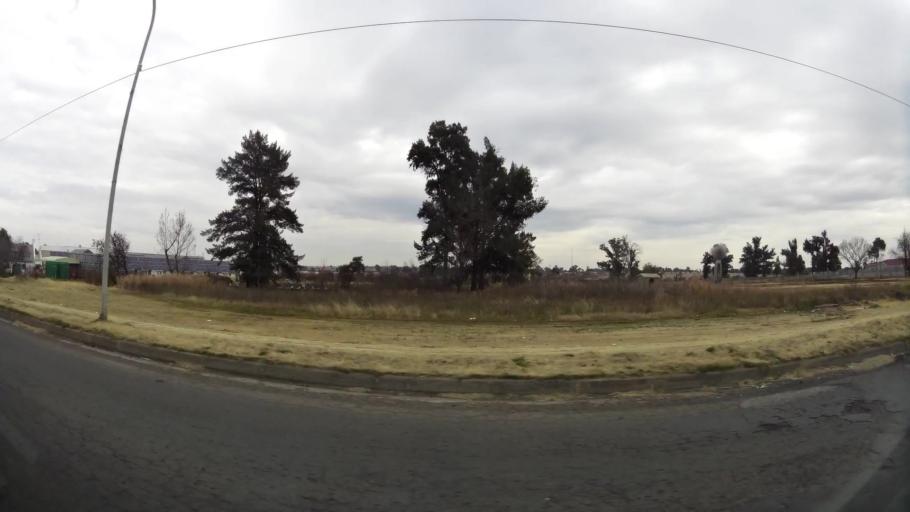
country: ZA
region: Orange Free State
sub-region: Fezile Dabi District Municipality
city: Kroonstad
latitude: -27.6515
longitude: 27.2313
